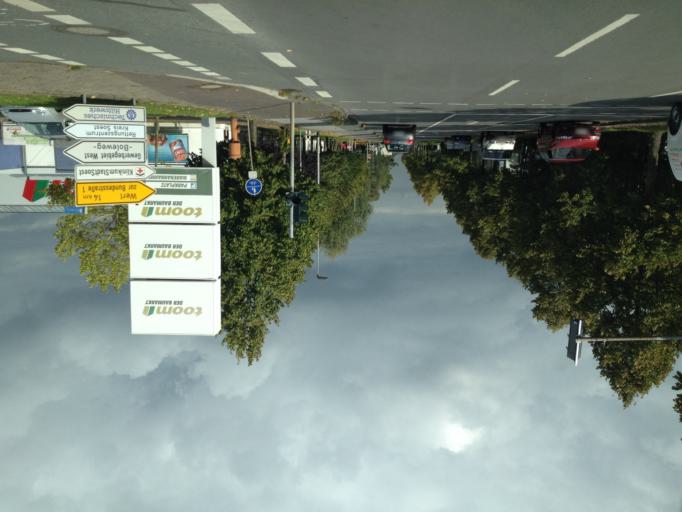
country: DE
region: North Rhine-Westphalia
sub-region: Regierungsbezirk Arnsberg
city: Soest
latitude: 51.5575
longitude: 8.0854
